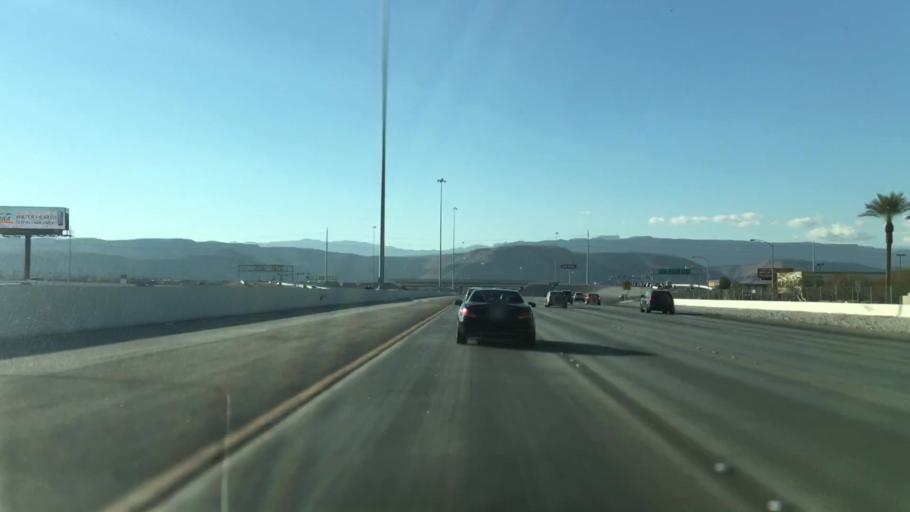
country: US
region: Nevada
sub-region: Clark County
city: Spring Valley
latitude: 36.0669
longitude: -115.2732
